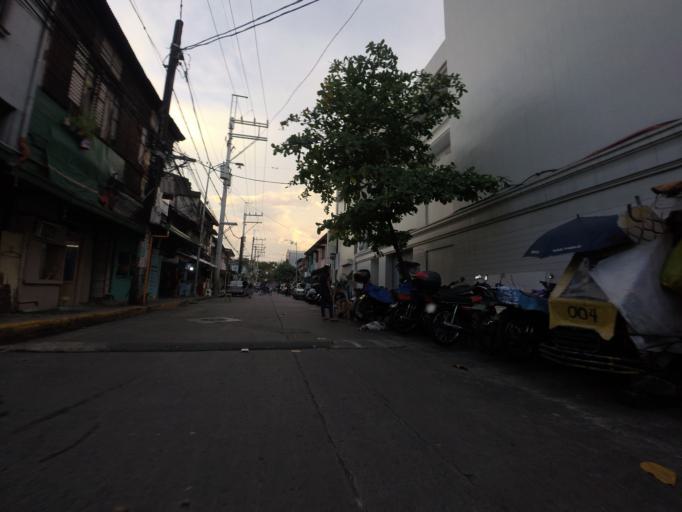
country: PH
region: Metro Manila
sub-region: City of Manila
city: Quiapo
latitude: 14.5926
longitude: 120.9898
